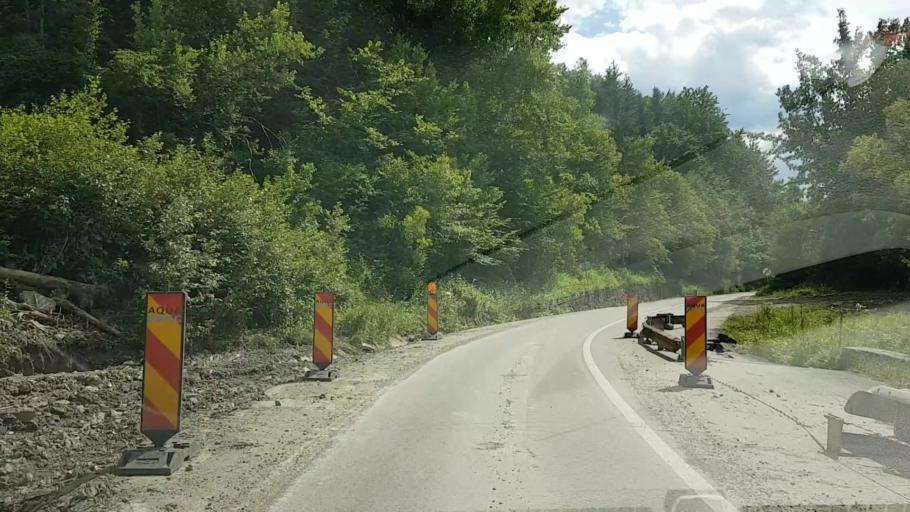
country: RO
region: Neamt
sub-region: Comuna Poiana Teiului
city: Poiana Teiului
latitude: 47.0790
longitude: 25.9682
